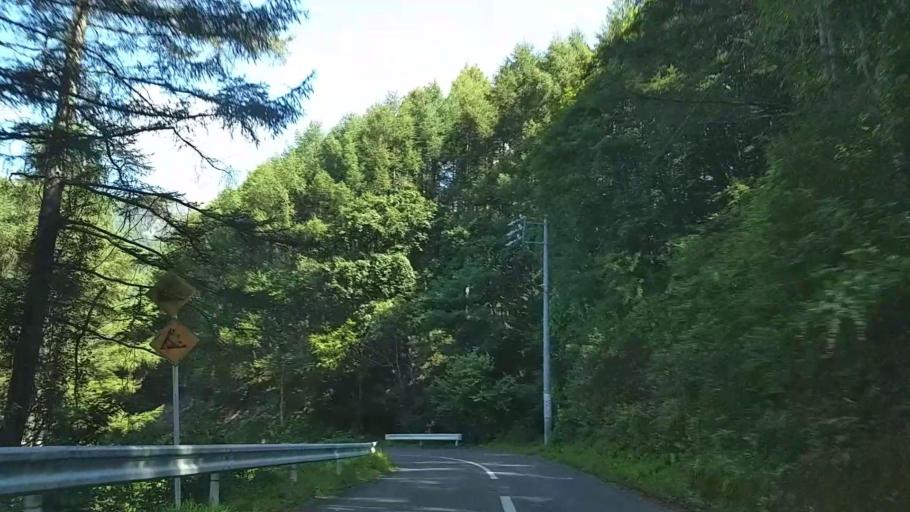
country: JP
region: Nagano
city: Matsumoto
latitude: 36.2034
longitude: 138.1051
